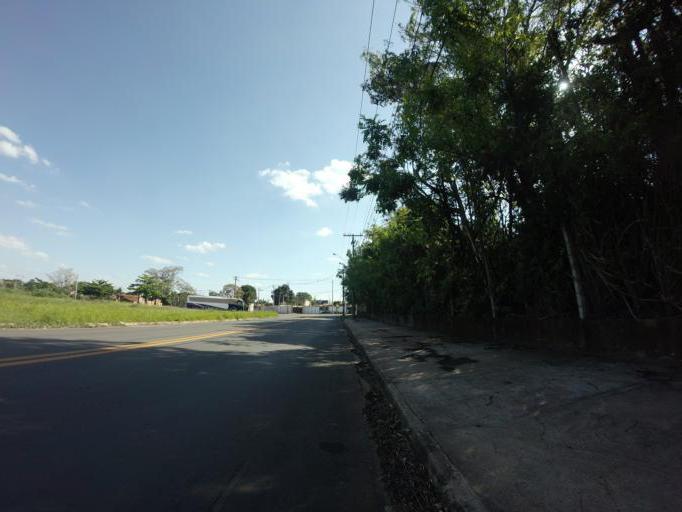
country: BR
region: Sao Paulo
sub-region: Piracicaba
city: Piracicaba
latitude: -22.7438
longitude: -47.5927
